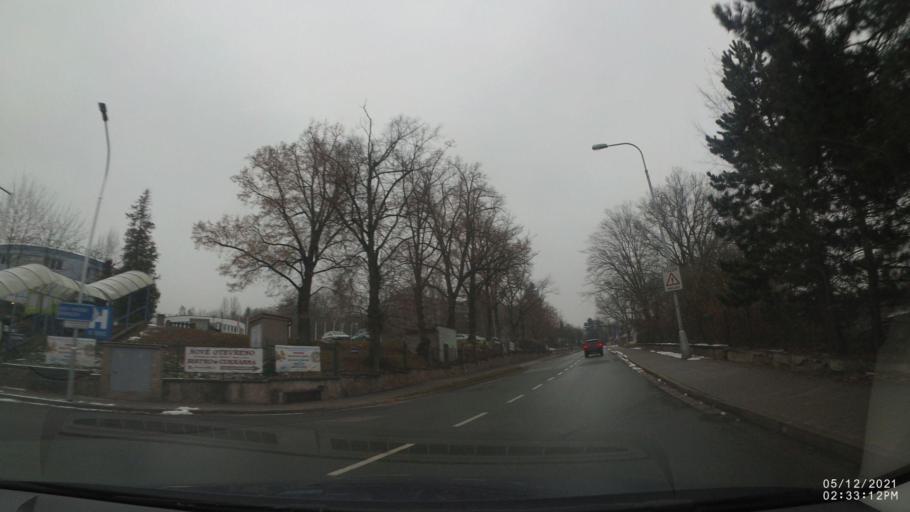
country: CZ
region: Kralovehradecky
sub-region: Okres Nachod
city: Nachod
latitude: 50.4109
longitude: 16.1651
